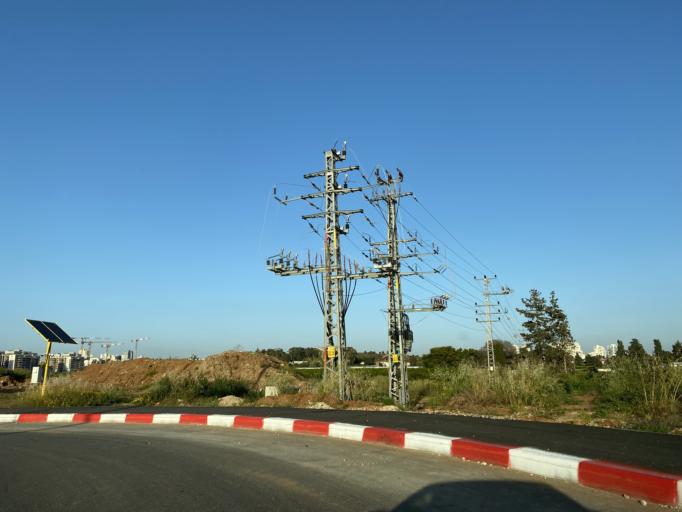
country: IL
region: Tel Aviv
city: Herzliyya
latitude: 32.1557
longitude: 34.8221
